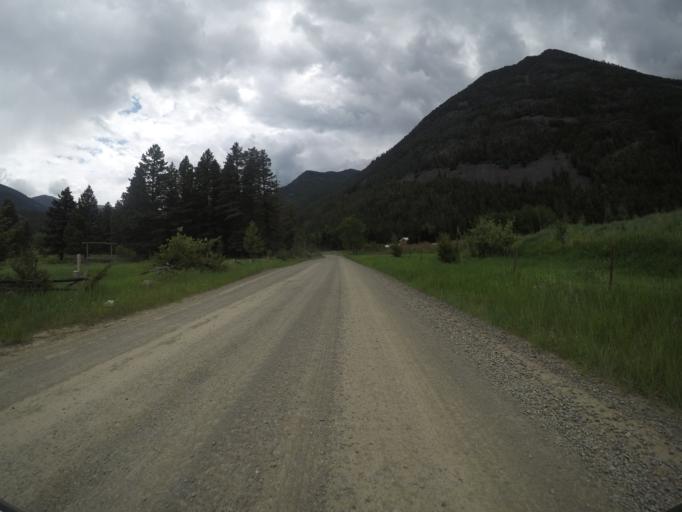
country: US
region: Montana
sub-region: Park County
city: Livingston
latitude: 45.4831
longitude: -110.2114
